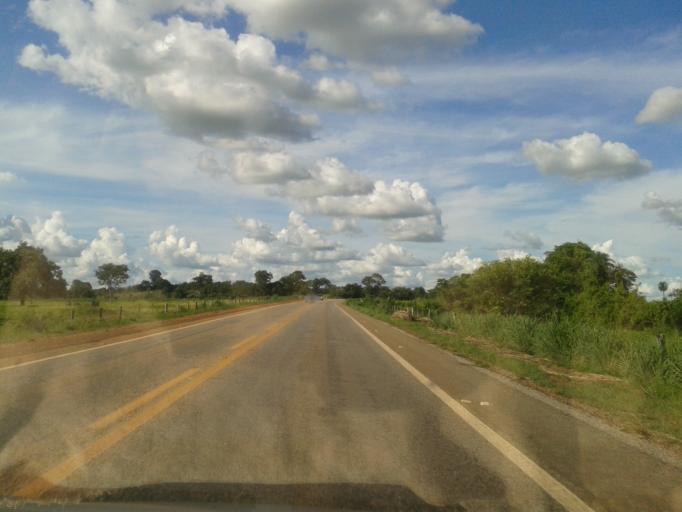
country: BR
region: Goias
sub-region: Mozarlandia
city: Mozarlandia
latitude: -14.7008
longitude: -50.5460
